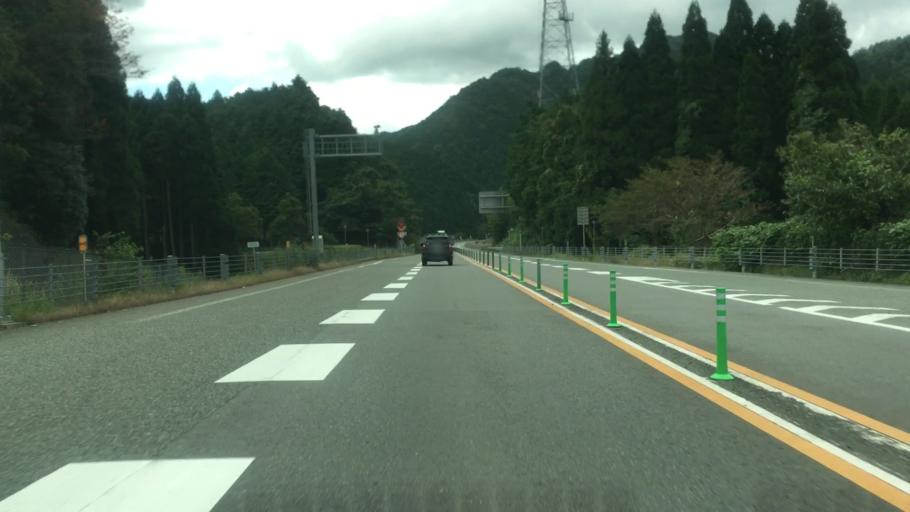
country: JP
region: Kyoto
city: Fukuchiyama
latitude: 35.2916
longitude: 134.9653
